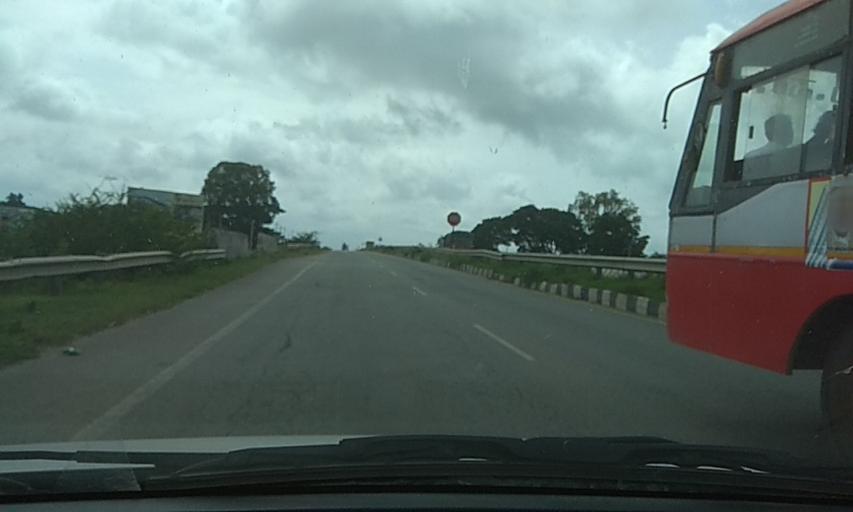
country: IN
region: Karnataka
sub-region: Davanagere
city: Harihar
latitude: 14.4558
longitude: 75.8664
